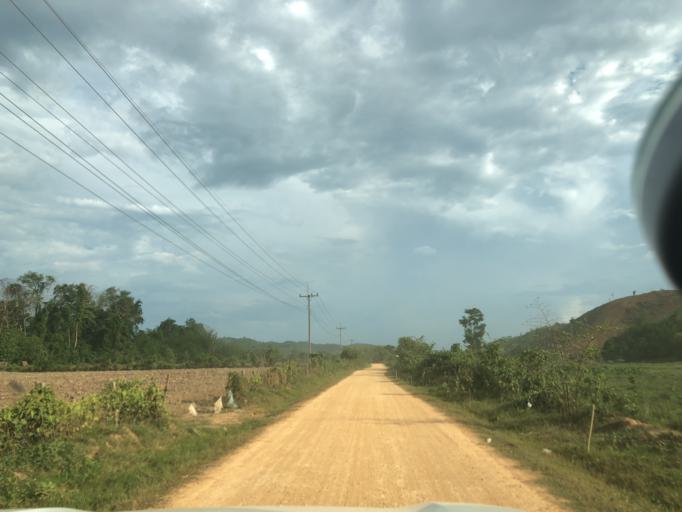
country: TH
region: Loei
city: Chiang Khan
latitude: 18.0095
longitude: 101.4204
